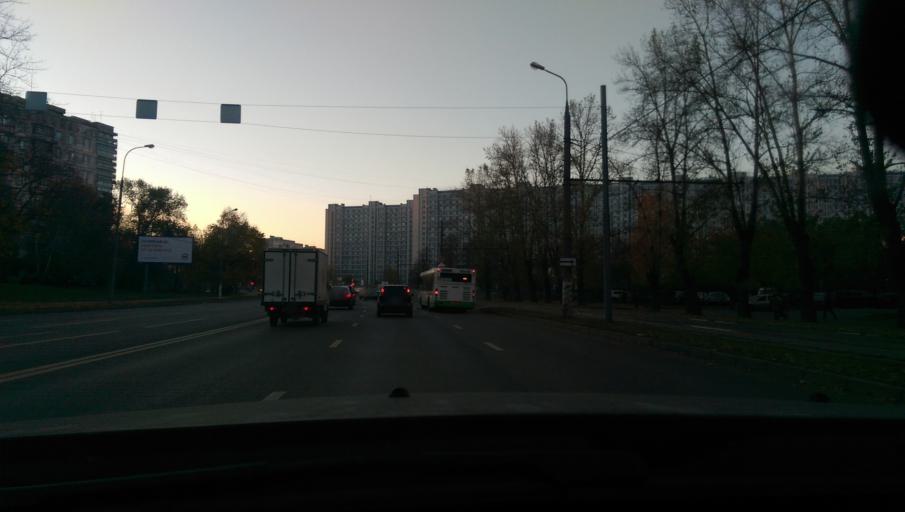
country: RU
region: Moscow
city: Leonovo
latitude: 55.8590
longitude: 37.6605
